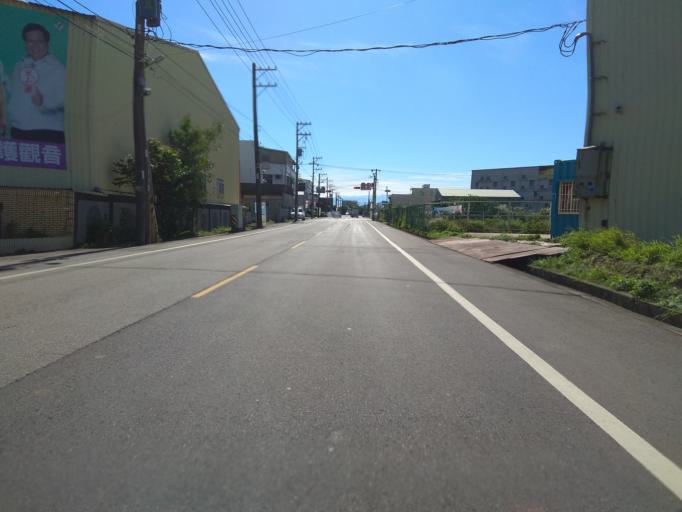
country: TW
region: Taiwan
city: Taoyuan City
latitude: 24.9827
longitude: 121.1354
